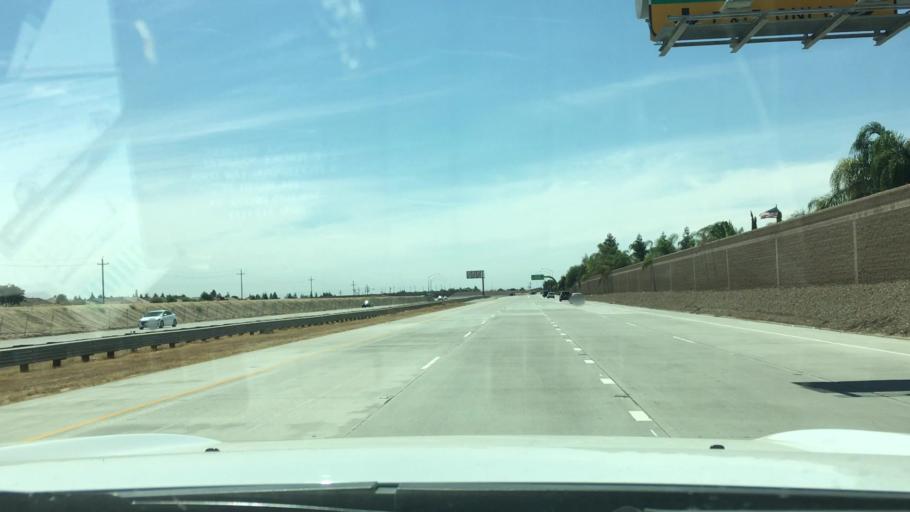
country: US
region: California
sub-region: Kern County
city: Rosedale
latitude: 35.3621
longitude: -119.1351
